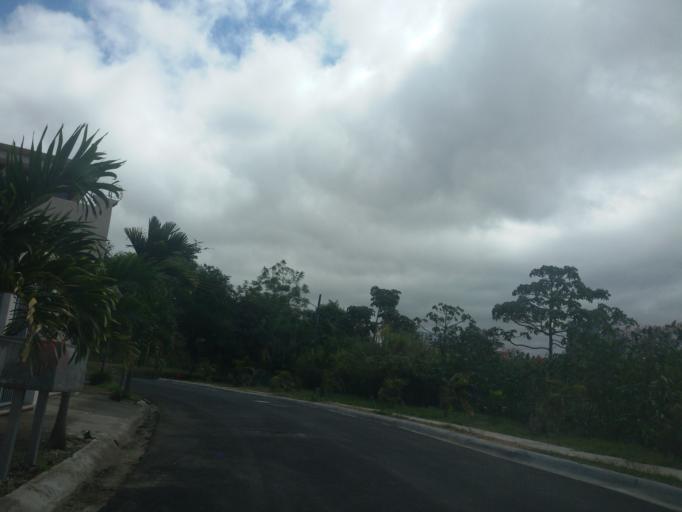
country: CR
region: San Jose
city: San Rafael
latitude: 9.9559
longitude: -84.1230
